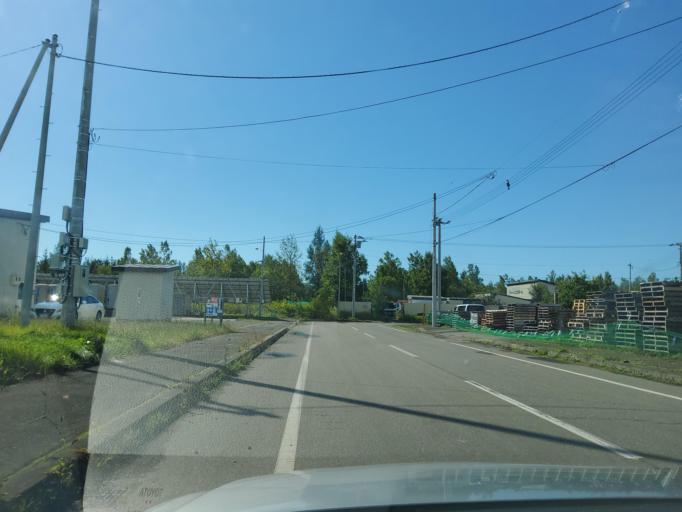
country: JP
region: Hokkaido
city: Otofuke
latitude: 42.9827
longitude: 143.1793
